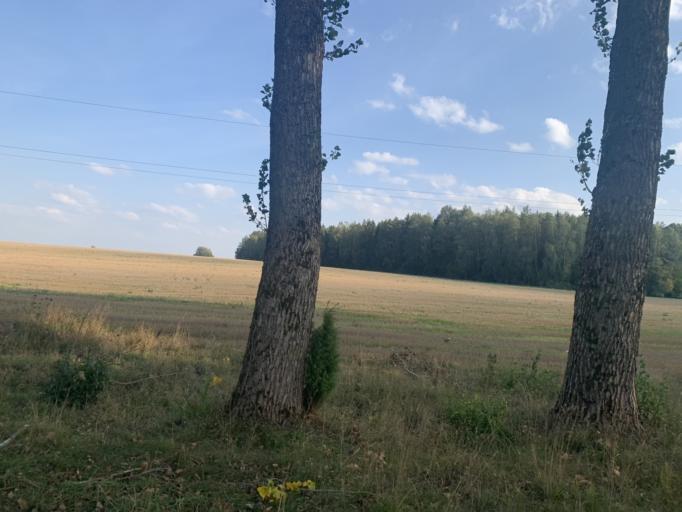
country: BY
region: Minsk
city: Ivyanyets
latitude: 53.8083
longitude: 26.6746
